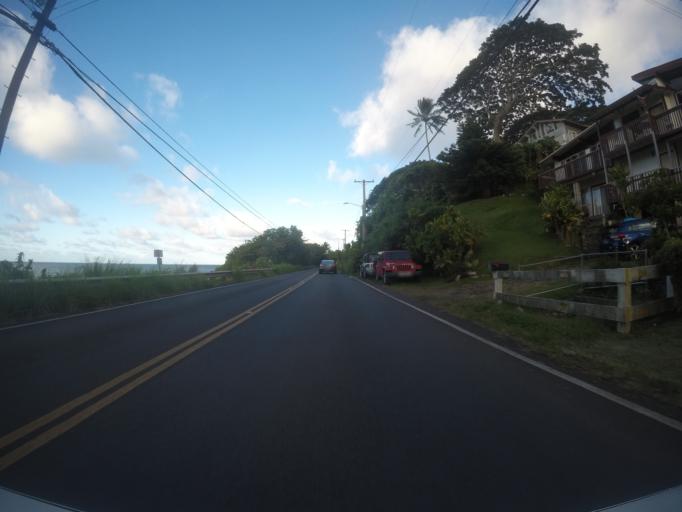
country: US
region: Hawaii
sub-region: Honolulu County
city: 'Ahuimanu
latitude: 21.4564
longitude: -157.8289
